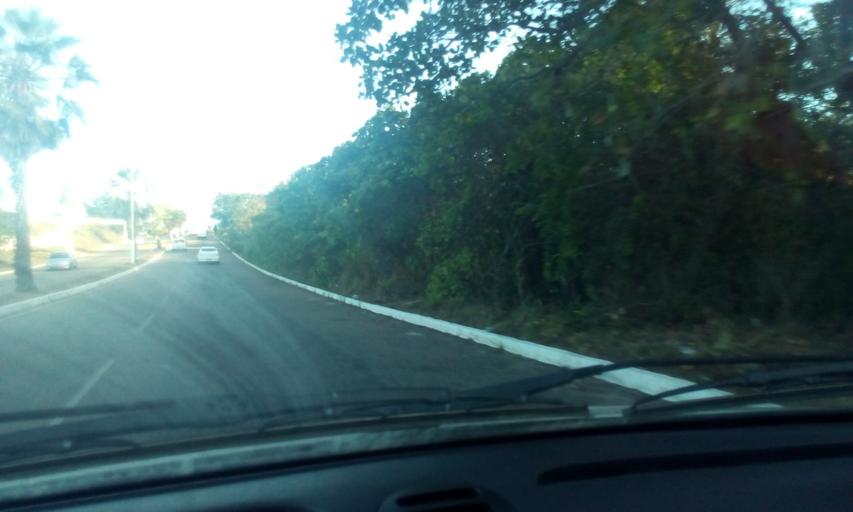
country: BR
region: Rio Grande do Norte
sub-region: Parnamirim
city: Parnamirim
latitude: -5.9675
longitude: -35.1411
